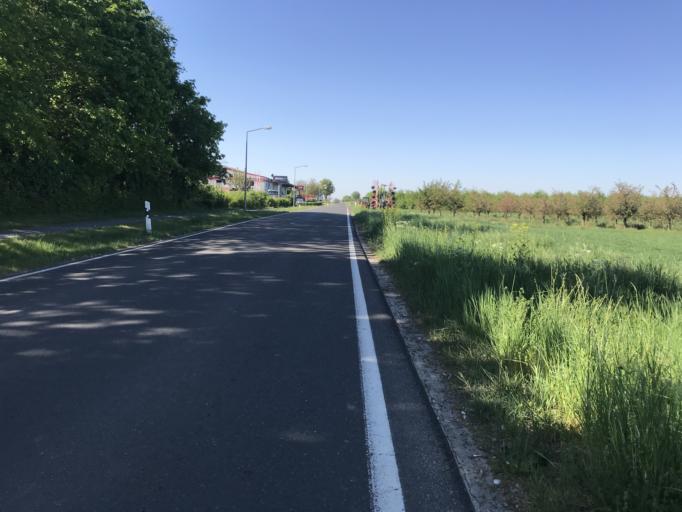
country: DE
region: Rheinland-Pfalz
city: Zornheim
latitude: 49.8835
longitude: 8.2211
